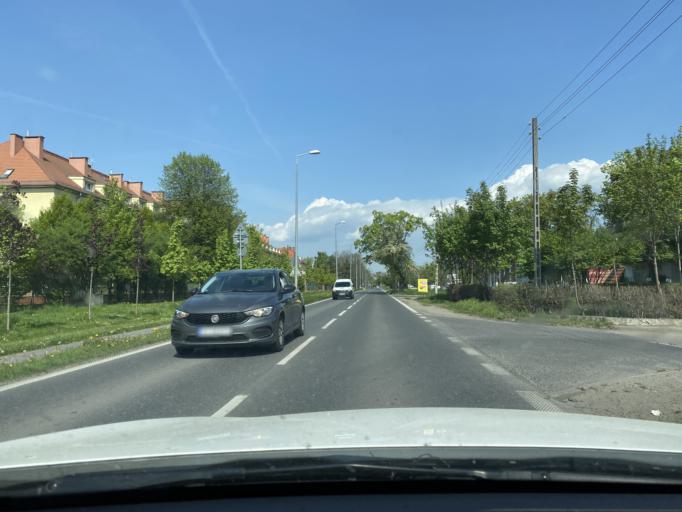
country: PL
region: Lower Silesian Voivodeship
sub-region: Powiat trzebnicki
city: Psary
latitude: 51.1449
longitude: 17.0234
